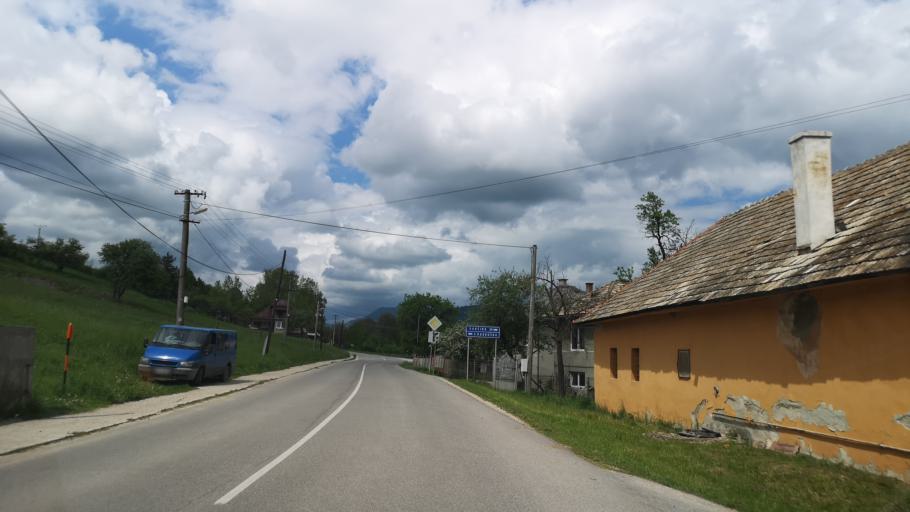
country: SK
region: Kosicky
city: Dobsina
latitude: 48.6902
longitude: 20.3471
